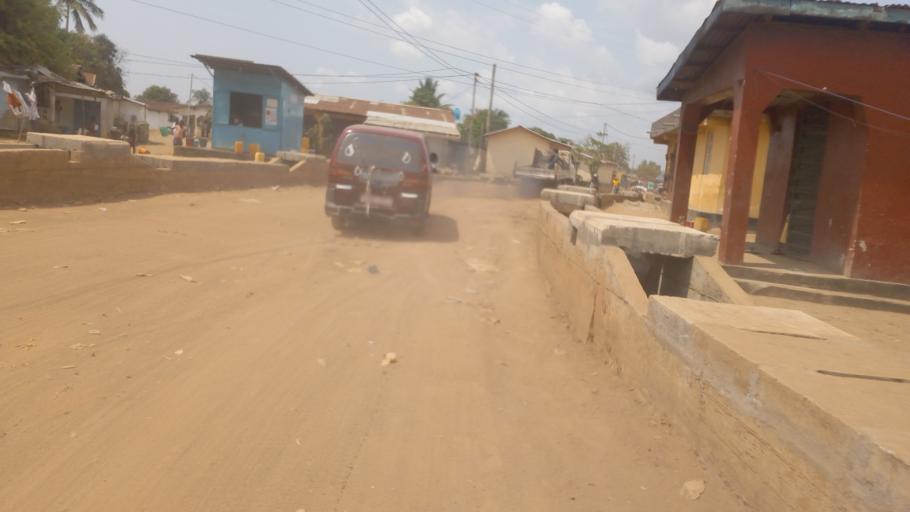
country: SL
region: Western Area
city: Waterloo
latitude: 8.3228
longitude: -13.0667
